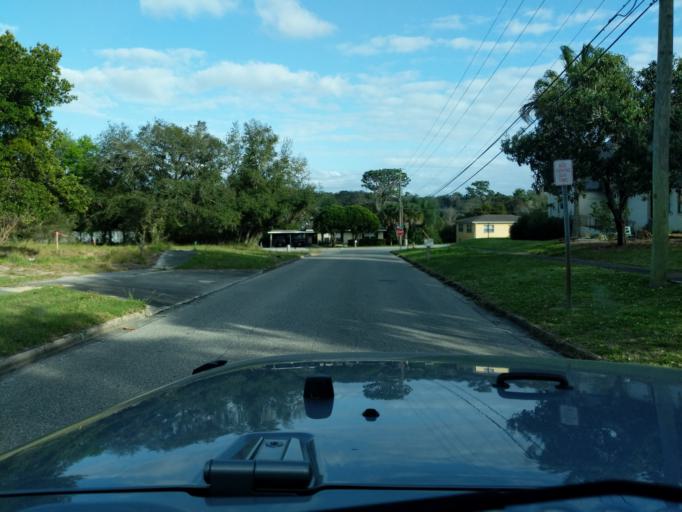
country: US
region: Florida
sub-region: Lake County
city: Clermont
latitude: 28.5502
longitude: -81.7578
